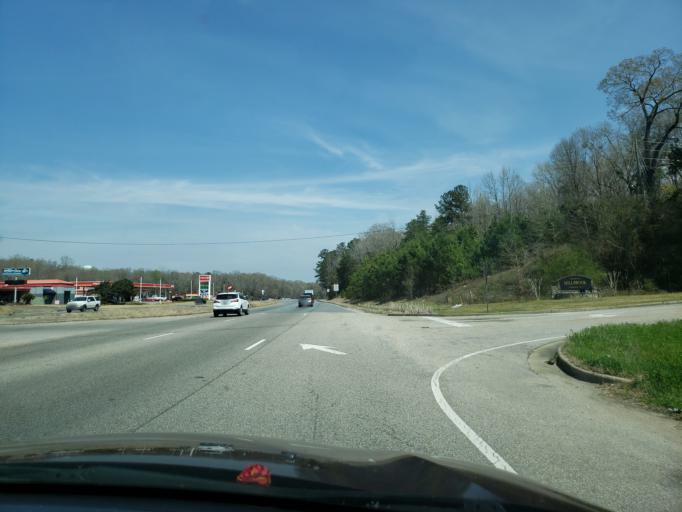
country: US
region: Alabama
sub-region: Elmore County
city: Millbrook
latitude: 32.4901
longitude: -86.4074
